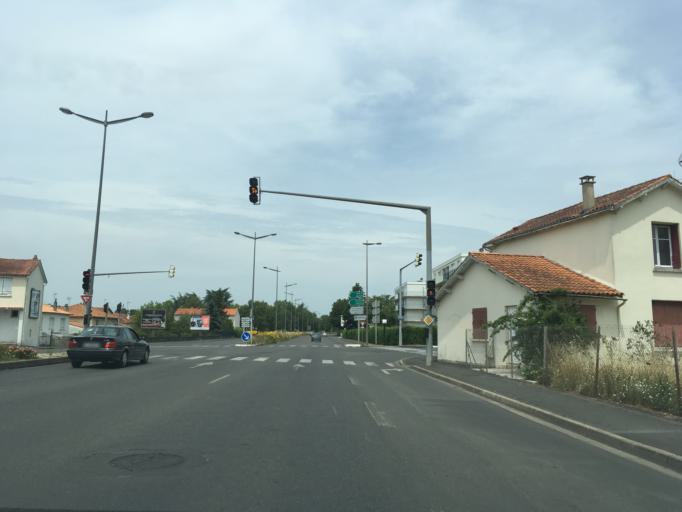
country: FR
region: Poitou-Charentes
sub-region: Departement des Deux-Sevres
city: Niort
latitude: 46.3192
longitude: -0.4858
